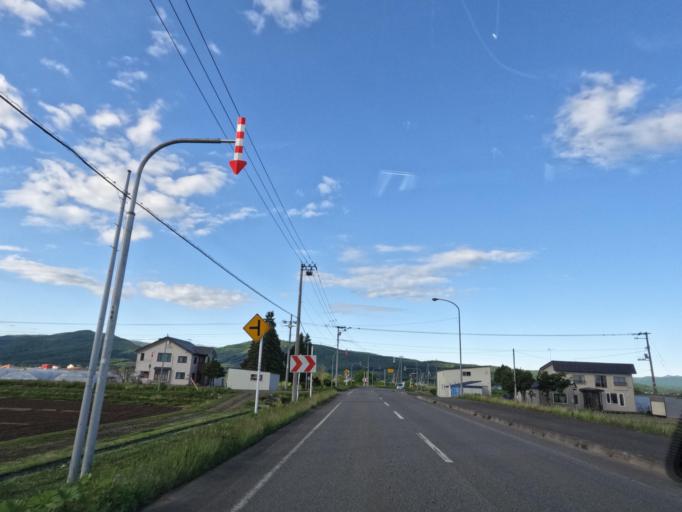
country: JP
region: Hokkaido
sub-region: Asahikawa-shi
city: Asahikawa
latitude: 43.8967
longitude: 142.4740
